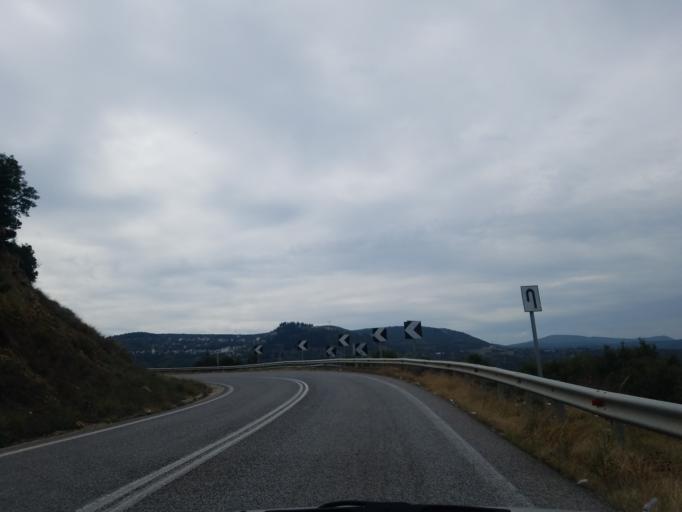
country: GR
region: Central Greece
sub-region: Nomos Fthiotidos
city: Domokos
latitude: 39.1424
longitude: 22.3081
